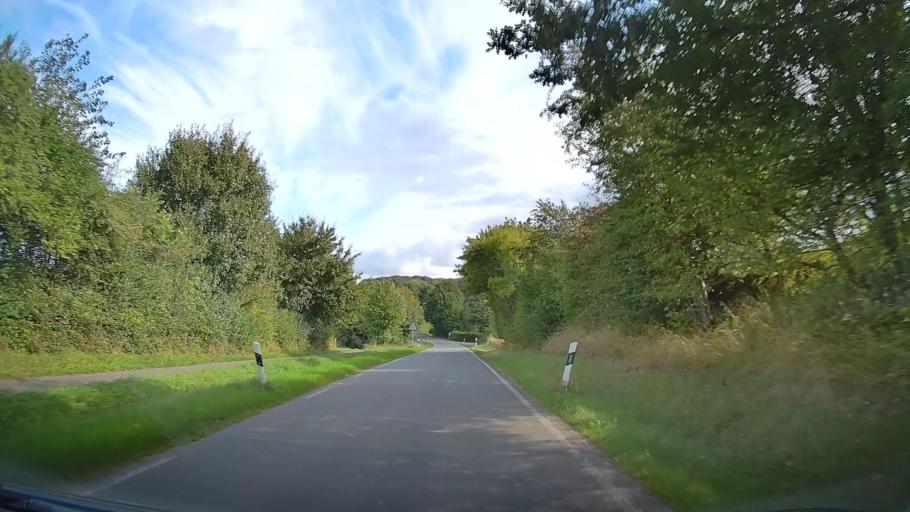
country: DE
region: Schleswig-Holstein
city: Dollerup
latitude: 54.8042
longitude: 9.6886
